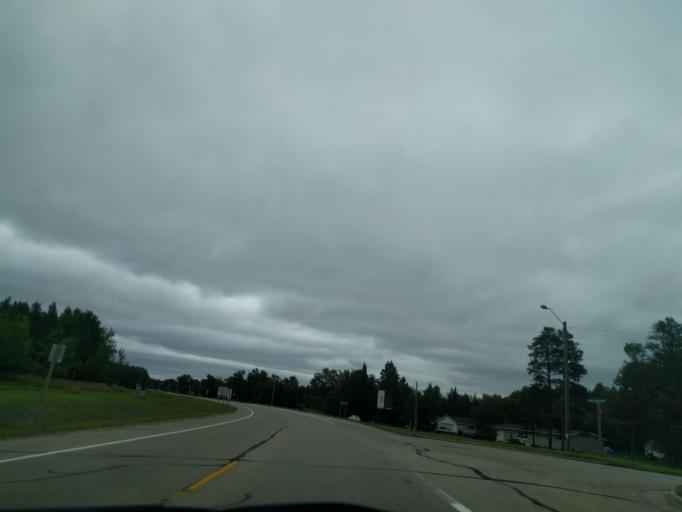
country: US
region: Michigan
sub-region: Delta County
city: Gladstone
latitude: 45.8556
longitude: -87.0583
